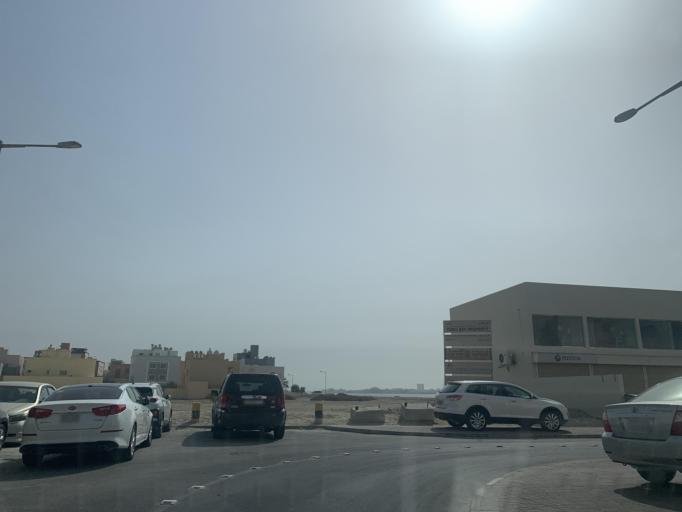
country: BH
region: Northern
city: Madinat `Isa
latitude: 26.1857
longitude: 50.5626
